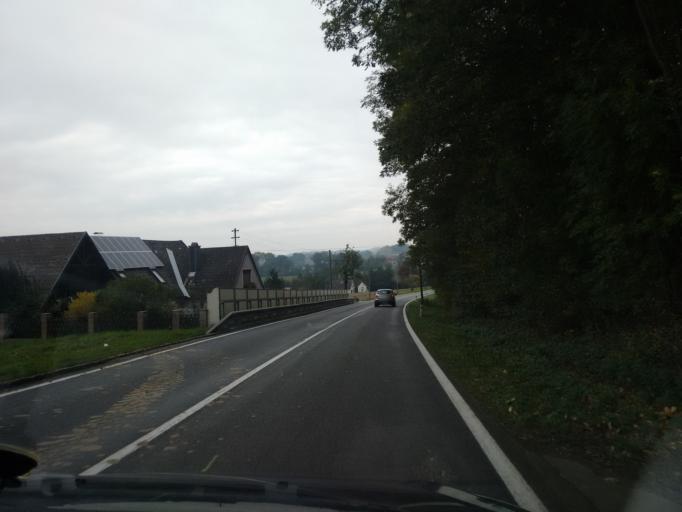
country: AT
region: Upper Austria
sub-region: Politischer Bezirk Kirchdorf an der Krems
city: Kremsmunster
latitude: 48.0583
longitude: 14.1644
